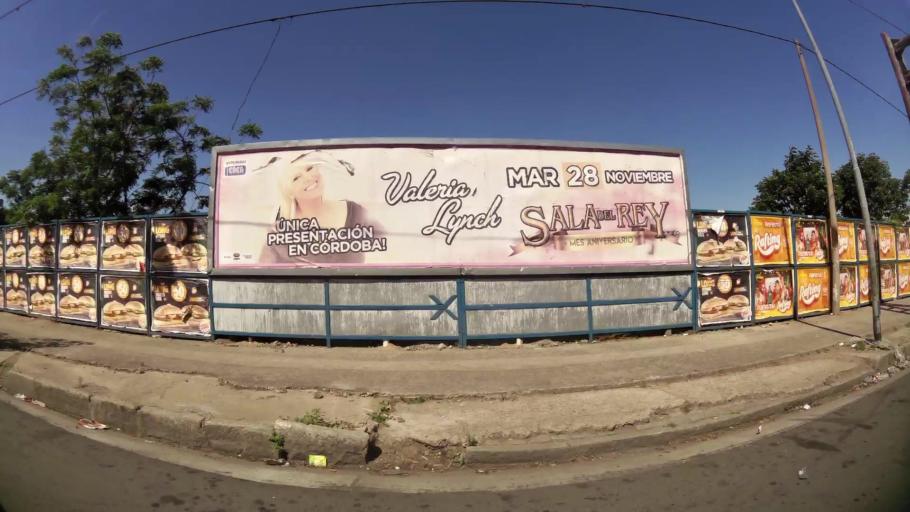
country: AR
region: Cordoba
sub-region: Departamento de Capital
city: Cordoba
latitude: -31.4091
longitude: -64.1730
